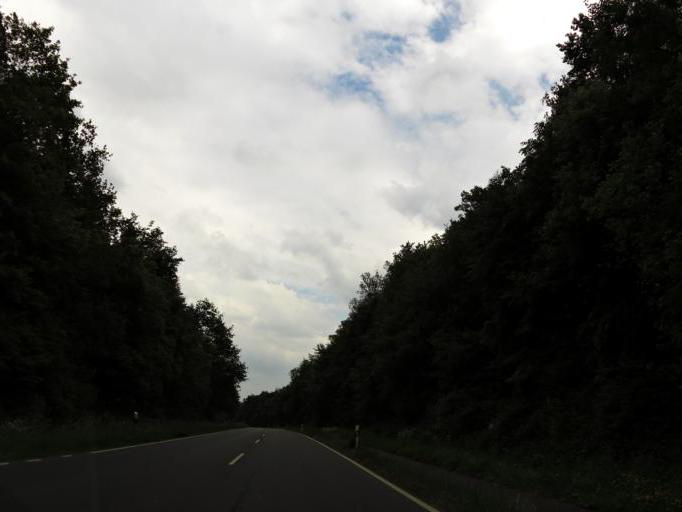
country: DE
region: Hesse
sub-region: Regierungsbezirk Darmstadt
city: Messel
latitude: 49.9079
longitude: 8.7778
